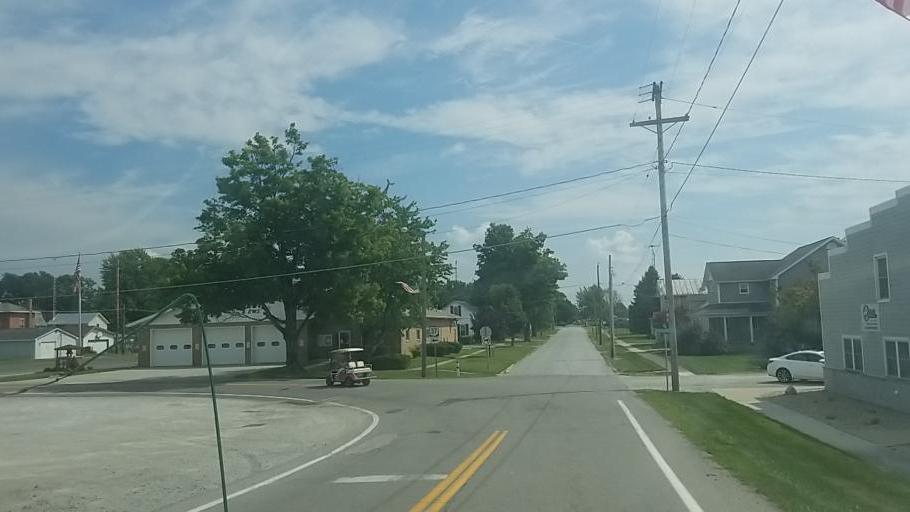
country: US
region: Ohio
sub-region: Hardin County
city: Forest
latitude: 40.8021
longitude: -83.5148
